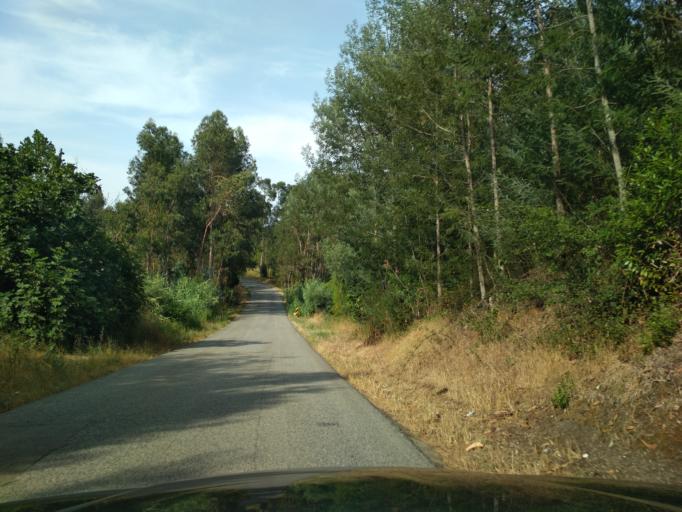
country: PT
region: Aveiro
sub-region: Mealhada
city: Mealhada
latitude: 40.3657
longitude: -8.5063
